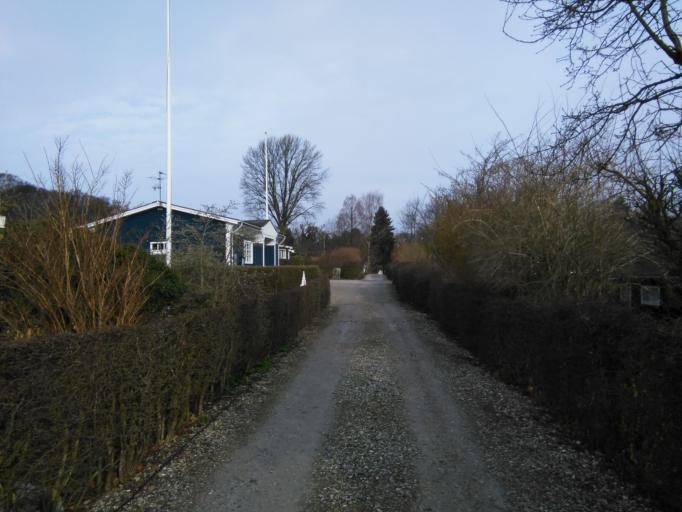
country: DK
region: Central Jutland
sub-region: Arhus Kommune
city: Arhus
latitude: 56.1233
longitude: 10.2023
